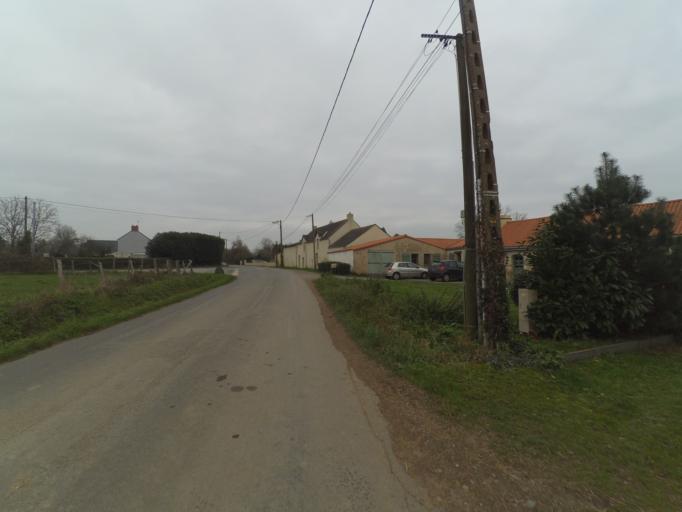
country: FR
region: Pays de la Loire
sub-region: Departement de la Loire-Atlantique
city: Coueron
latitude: 47.2311
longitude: -1.6908
